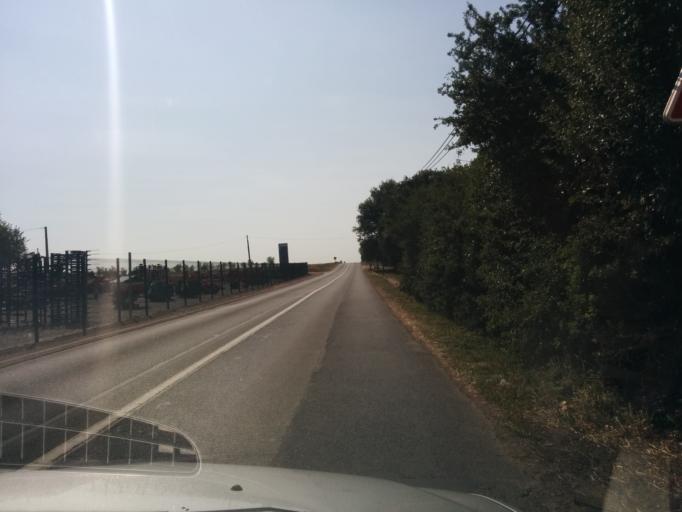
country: FR
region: Poitou-Charentes
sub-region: Departement de la Vienne
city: Moncontour
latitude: 46.8071
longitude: 0.0151
